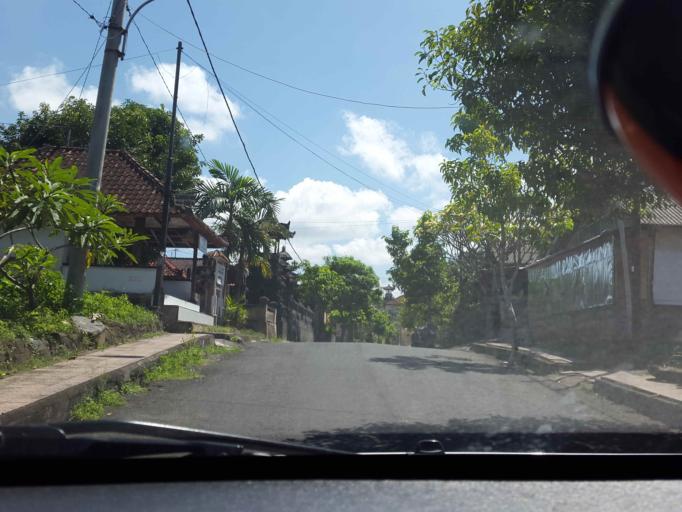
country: ID
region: Bali
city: Klungkung
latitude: -8.5357
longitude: 115.3947
